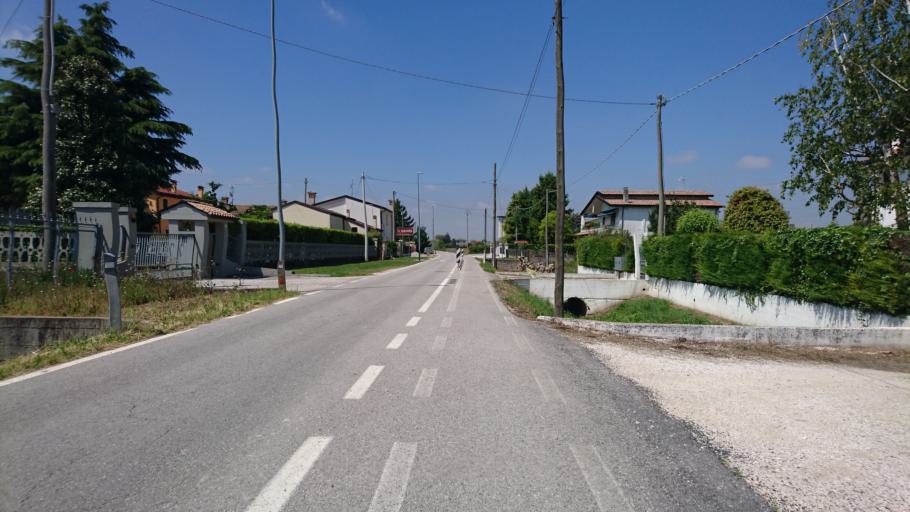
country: IT
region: Veneto
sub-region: Provincia di Padova
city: Albignasego
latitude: 45.3375
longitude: 11.8981
